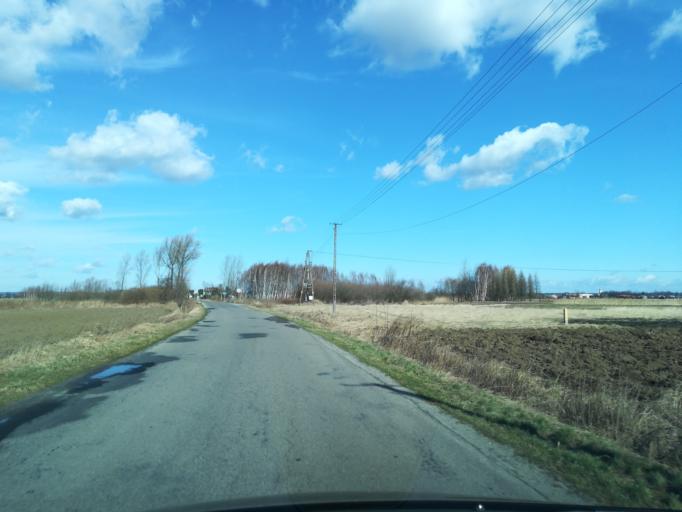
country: PL
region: Subcarpathian Voivodeship
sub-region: Powiat lancucki
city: Bialobrzegi
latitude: 50.0890
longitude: 22.3214
